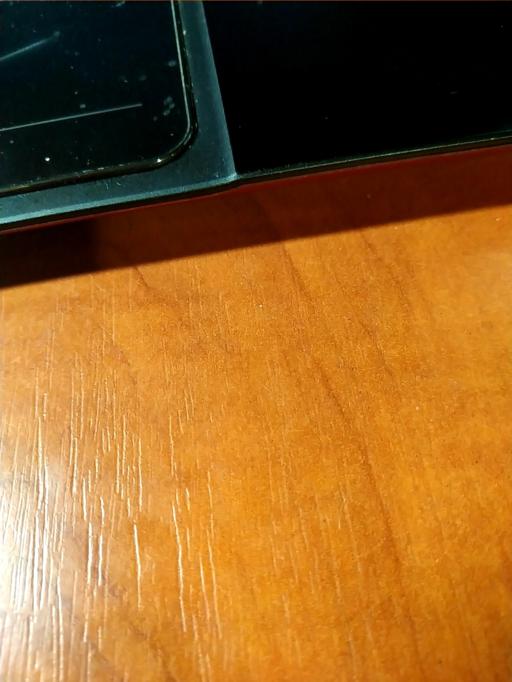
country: RU
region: Tverskaya
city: Zubtsov
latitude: 56.3284
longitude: 34.6748
